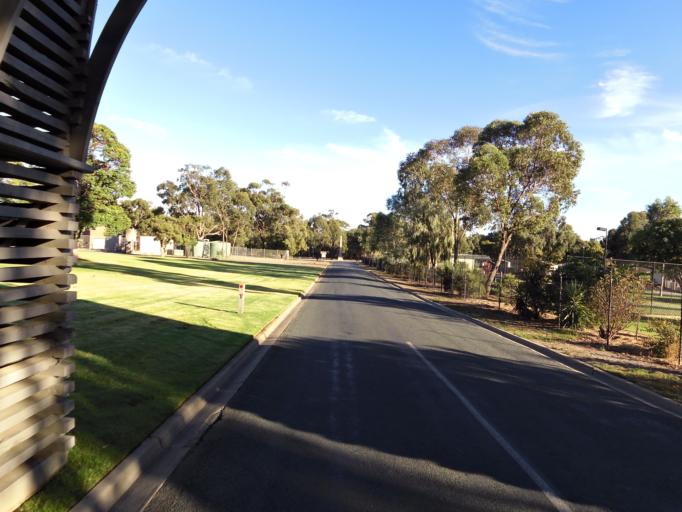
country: AU
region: New South Wales
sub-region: Murray Shire
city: Moama
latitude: -36.1163
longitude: 144.7427
